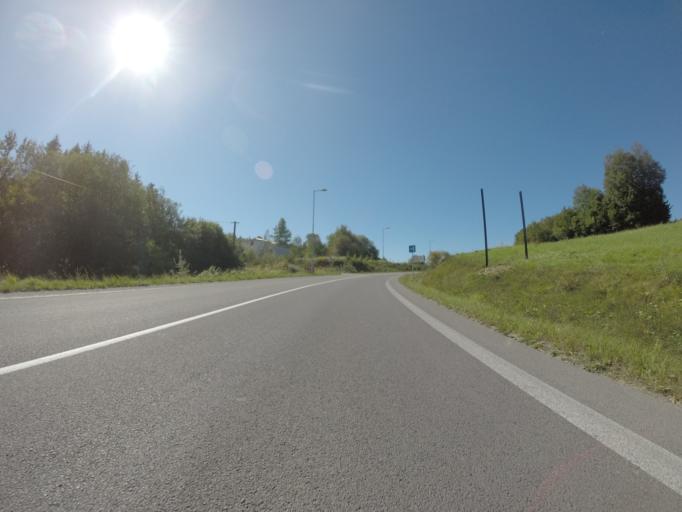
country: SK
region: Trenciansky
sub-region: Okres Povazska Bystrica
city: Povazska Bystrica
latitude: 49.1008
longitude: 18.4527
